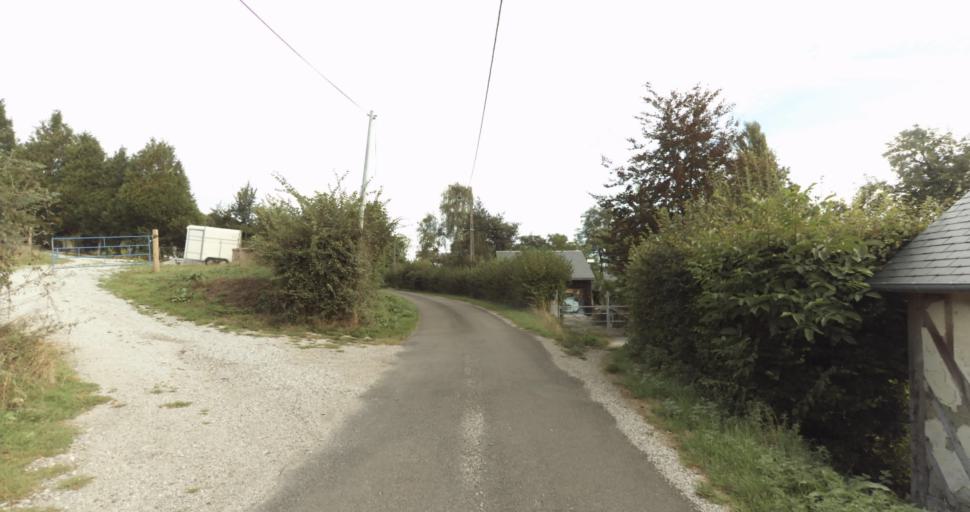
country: FR
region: Lower Normandy
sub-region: Departement de l'Orne
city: Gace
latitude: 48.8348
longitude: 0.2228
